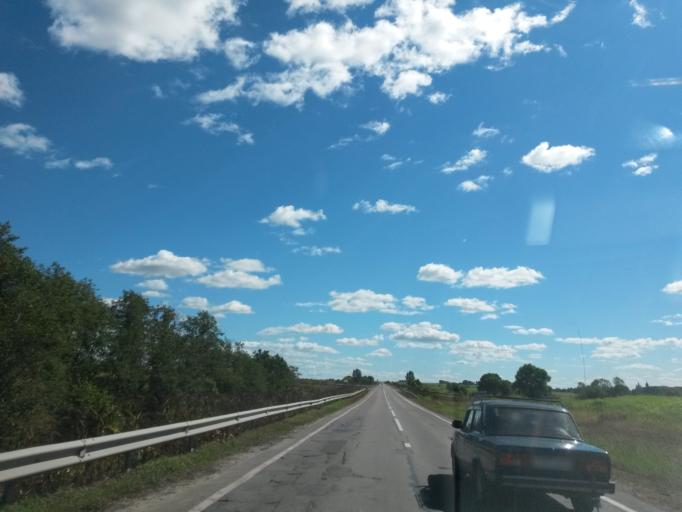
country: RU
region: Jaroslavl
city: Yaroslavl
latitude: 57.7801
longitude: 39.8453
